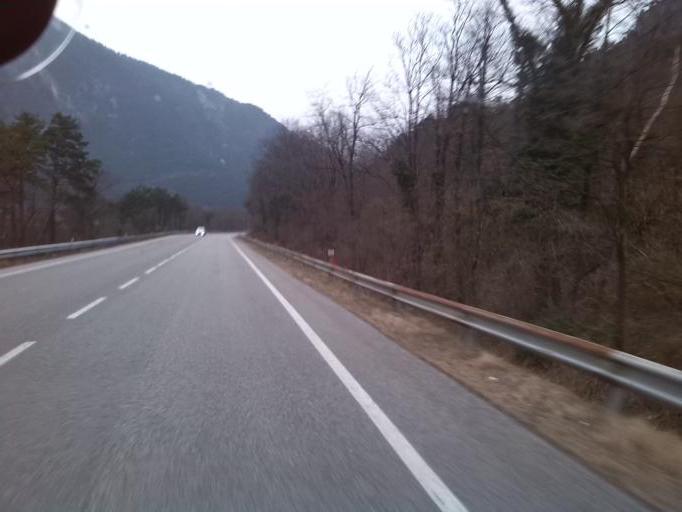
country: IT
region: Friuli Venezia Giulia
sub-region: Provincia di Udine
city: Moggio di Sotto
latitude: 46.3909
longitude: 13.1636
